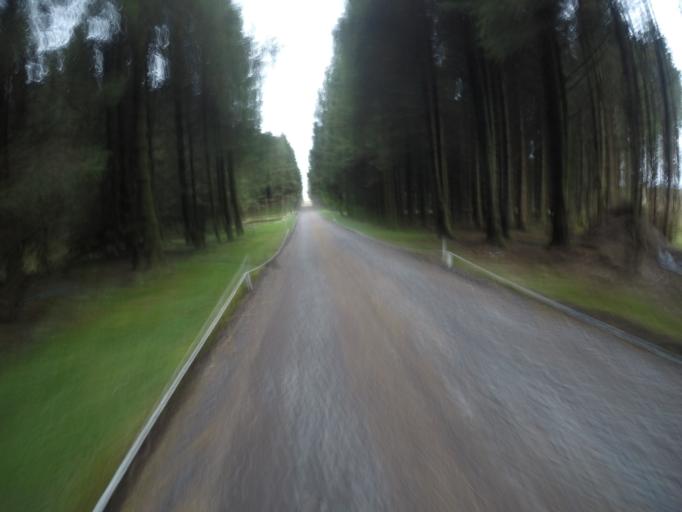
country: GB
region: Scotland
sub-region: East Ayrshire
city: Galston
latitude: 55.6757
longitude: -4.3684
